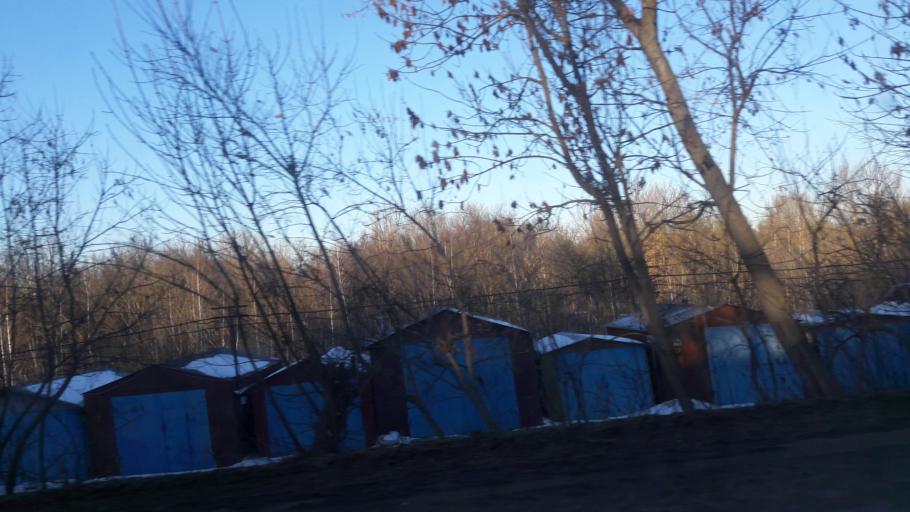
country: RU
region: Tula
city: Tula
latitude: 54.2215
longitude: 37.6497
